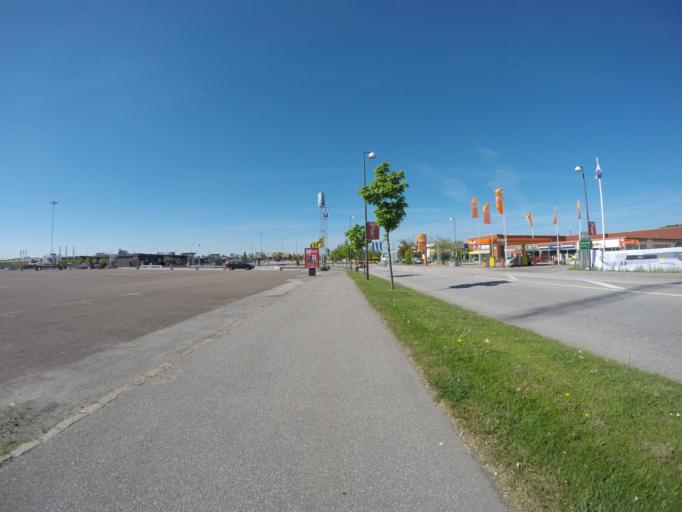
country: SE
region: Skane
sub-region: Malmo
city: Oxie
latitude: 55.5726
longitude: 13.0583
